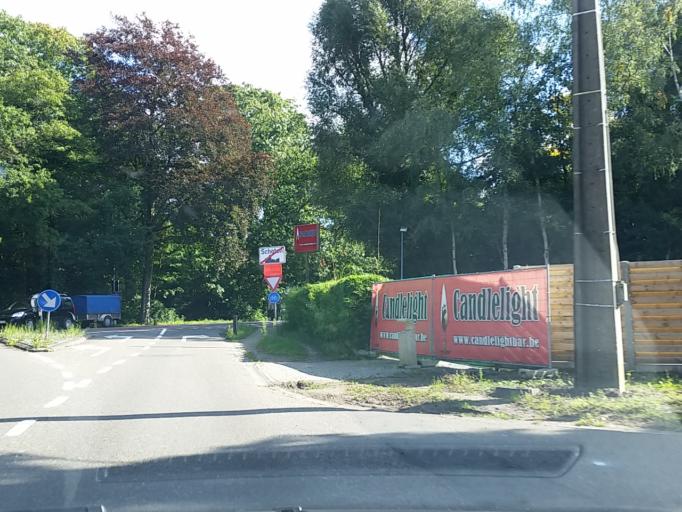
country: BE
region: Flanders
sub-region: Provincie Antwerpen
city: Schoten
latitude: 51.2641
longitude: 4.5453
